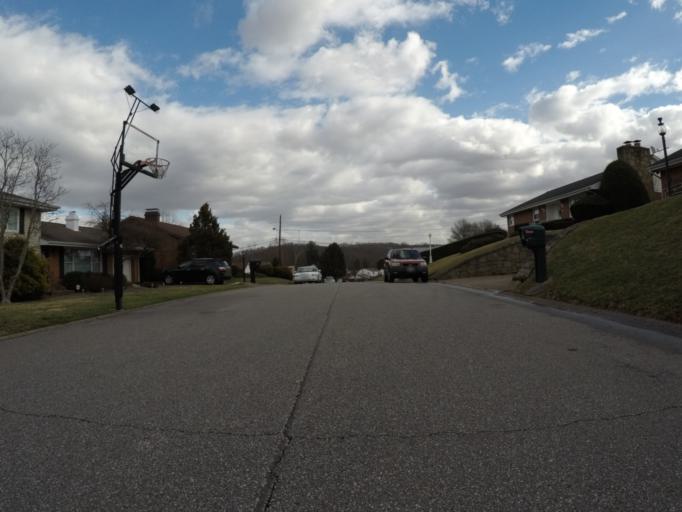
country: US
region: West Virginia
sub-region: Cabell County
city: Huntington
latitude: 38.4083
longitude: -82.3876
